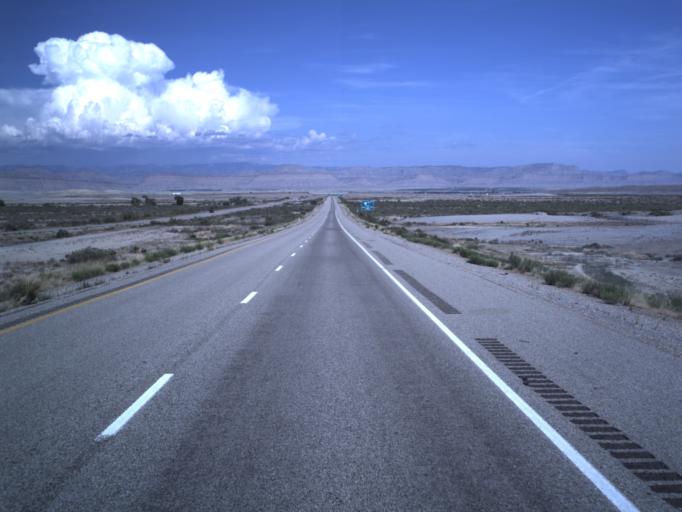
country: US
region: Utah
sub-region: Carbon County
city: East Carbon City
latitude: 38.9743
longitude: -110.2521
